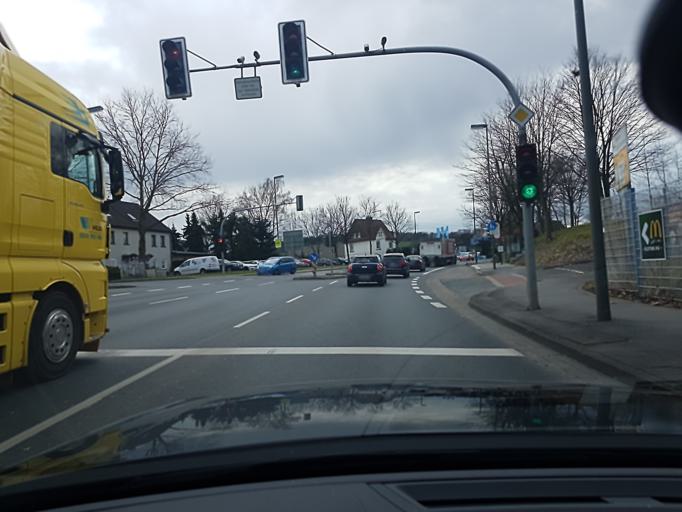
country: DE
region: North Rhine-Westphalia
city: Iserlohn
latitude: 51.4025
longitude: 7.6987
